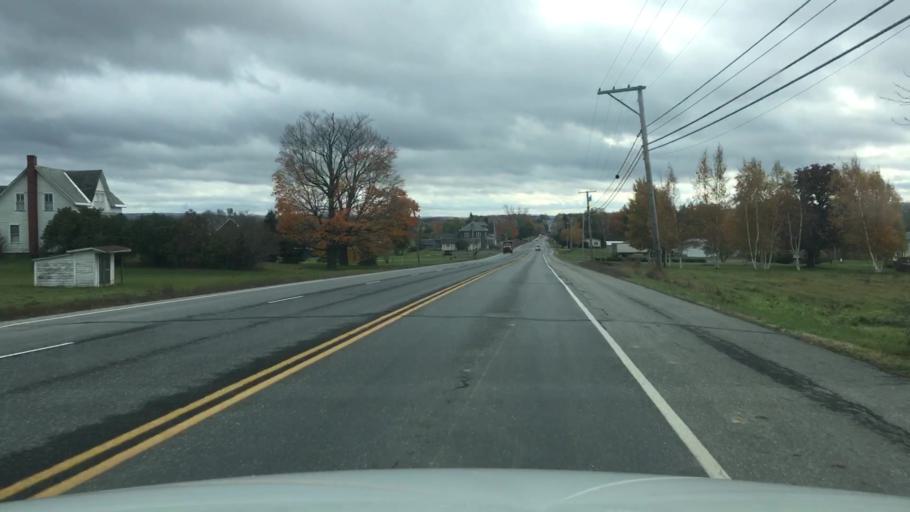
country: US
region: Maine
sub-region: Aroostook County
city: Houlton
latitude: 46.2202
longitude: -67.8411
